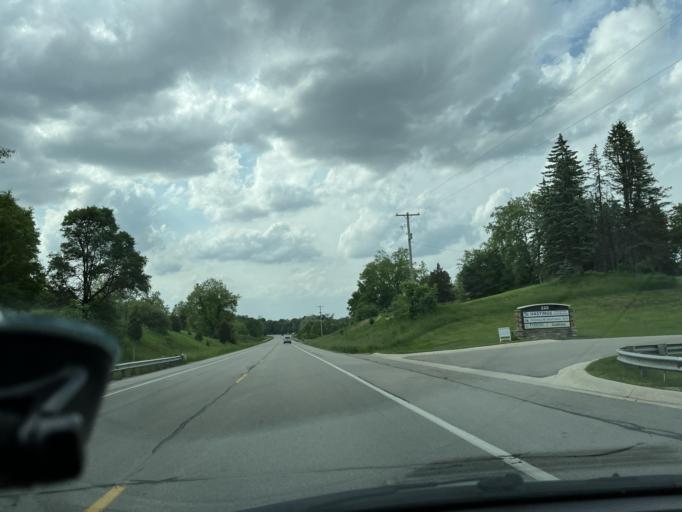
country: US
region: Michigan
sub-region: Barry County
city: Hastings
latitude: 42.6494
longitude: -85.3395
